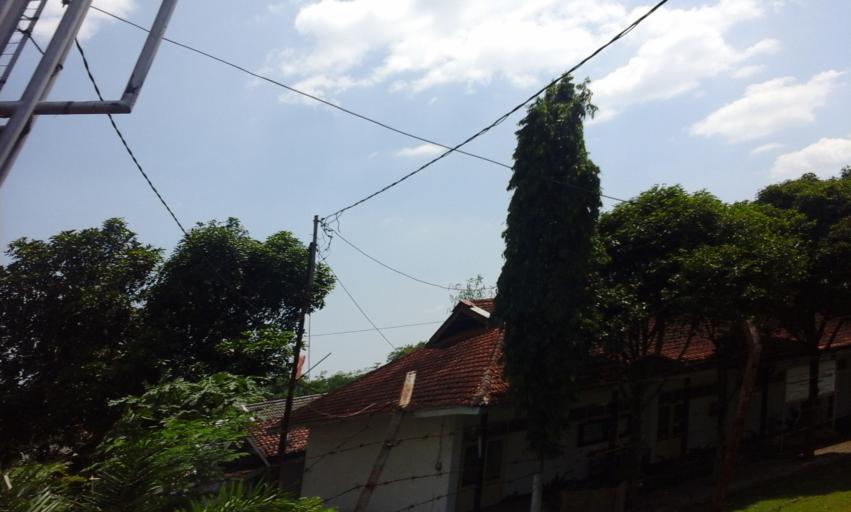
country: ID
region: East Java
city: Patrang
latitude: -8.1499
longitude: 113.7111
